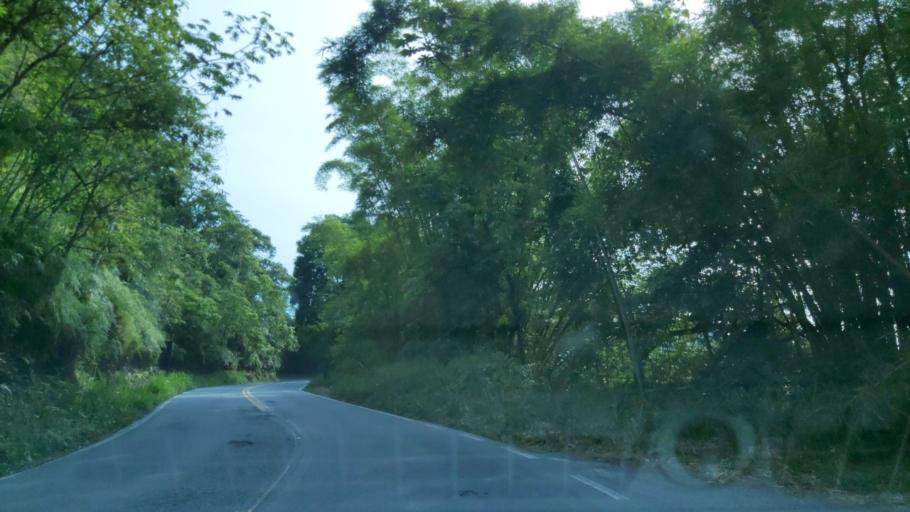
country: BR
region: Sao Paulo
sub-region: Juquia
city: Juquia
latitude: -24.1107
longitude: -47.6279
